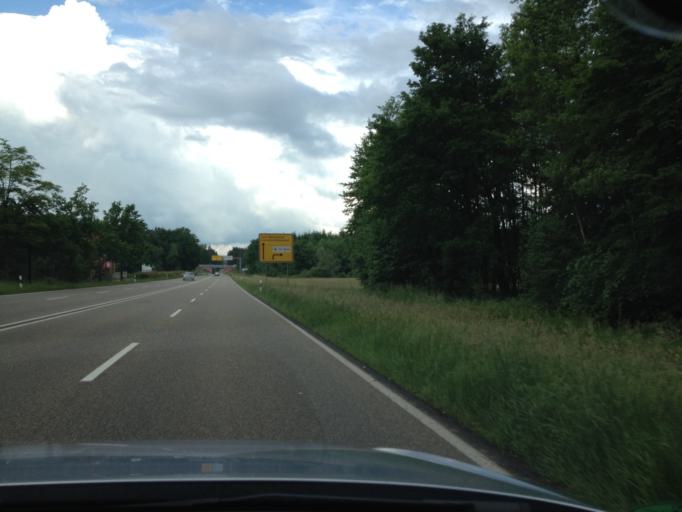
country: DE
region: Rheinland-Pfalz
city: Ramstein-Miesenbach
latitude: 49.4280
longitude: 7.5556
